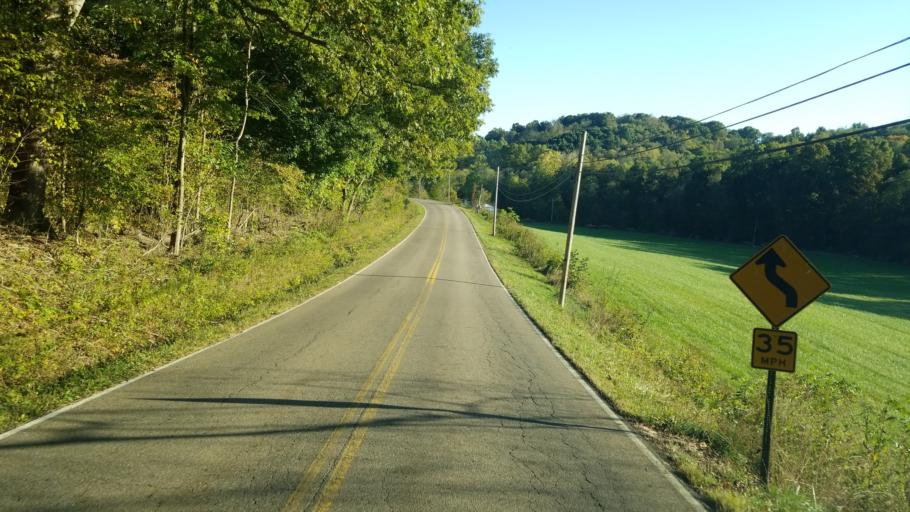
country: US
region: Ohio
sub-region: Licking County
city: Utica
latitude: 40.1695
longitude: -82.3881
